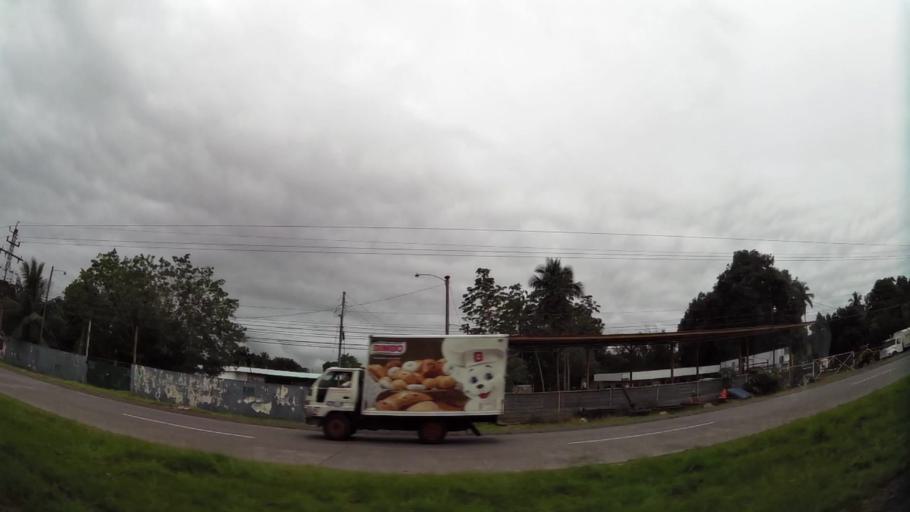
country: PA
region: Chiriqui
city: Tijera
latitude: 8.4696
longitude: -82.5331
